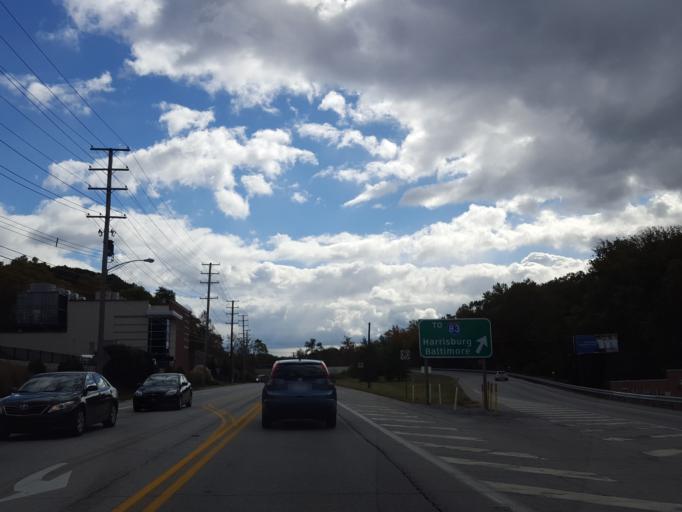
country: US
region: Pennsylvania
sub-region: York County
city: Grantley
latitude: 39.9449
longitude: -76.7195
